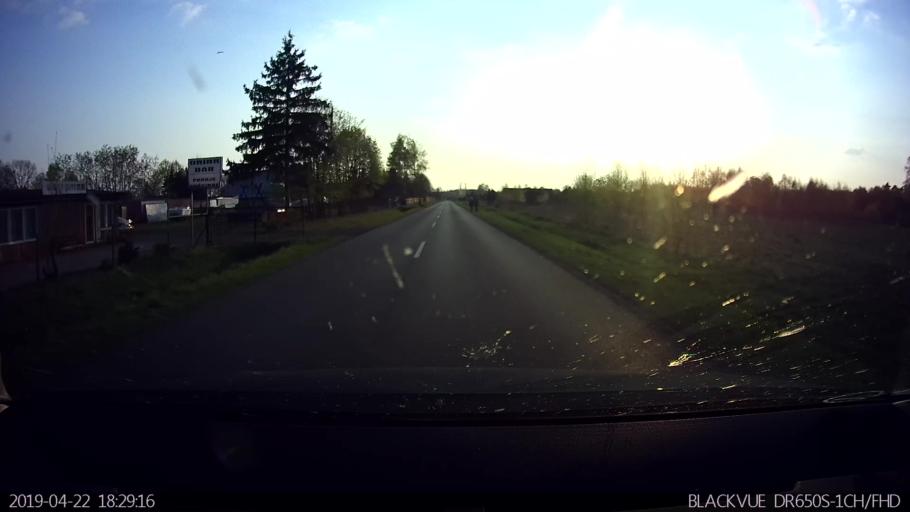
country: PL
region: Masovian Voivodeship
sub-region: Powiat wolominski
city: Tluszcz
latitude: 52.4537
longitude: 21.4554
